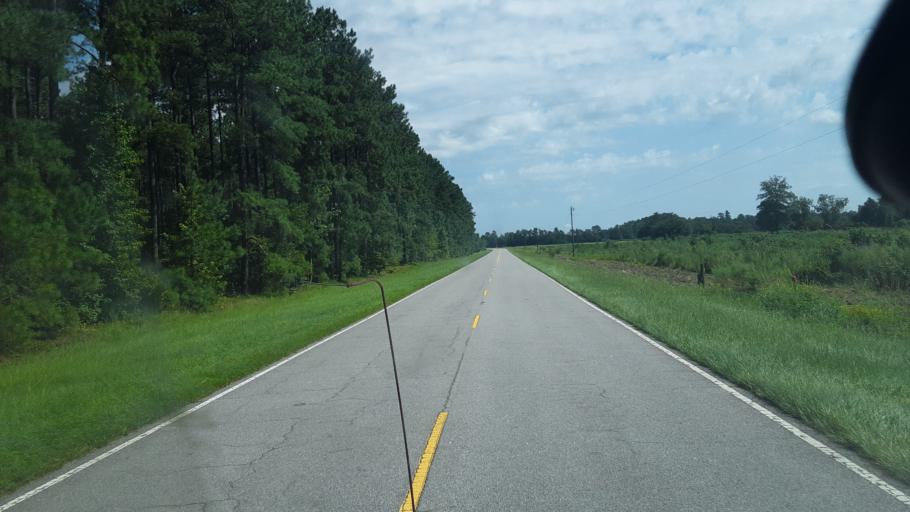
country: US
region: South Carolina
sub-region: Hampton County
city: Hampton
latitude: 33.0348
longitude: -81.0373
